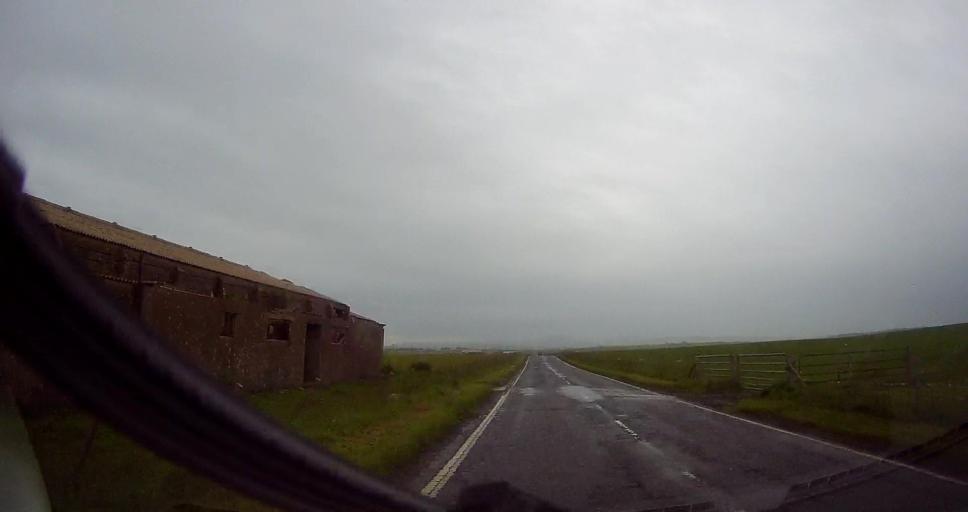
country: GB
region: Scotland
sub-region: Orkney Islands
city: Stromness
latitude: 59.0664
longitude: -3.2808
